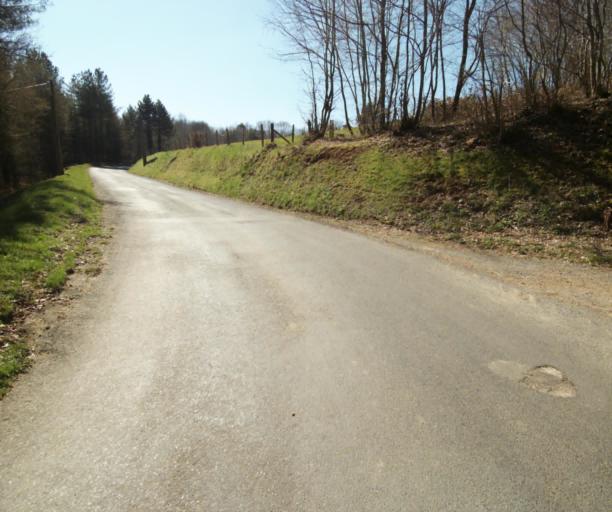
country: FR
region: Limousin
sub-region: Departement de la Correze
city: Naves
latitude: 45.3082
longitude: 1.7199
